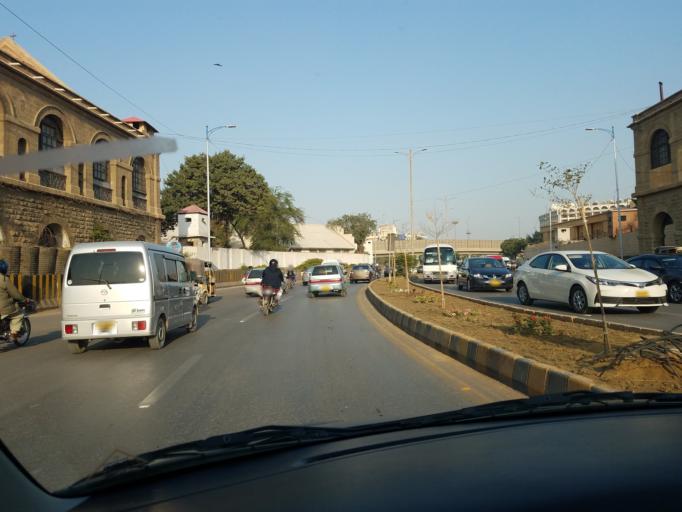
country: PK
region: Sindh
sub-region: Karachi District
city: Karachi
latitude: 24.8550
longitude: 67.0362
